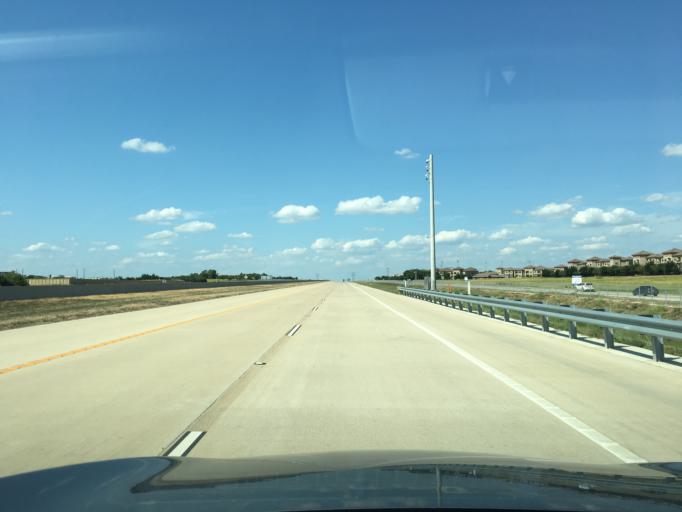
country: US
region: Texas
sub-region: Tarrant County
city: Mansfield
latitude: 32.5641
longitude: -97.0841
